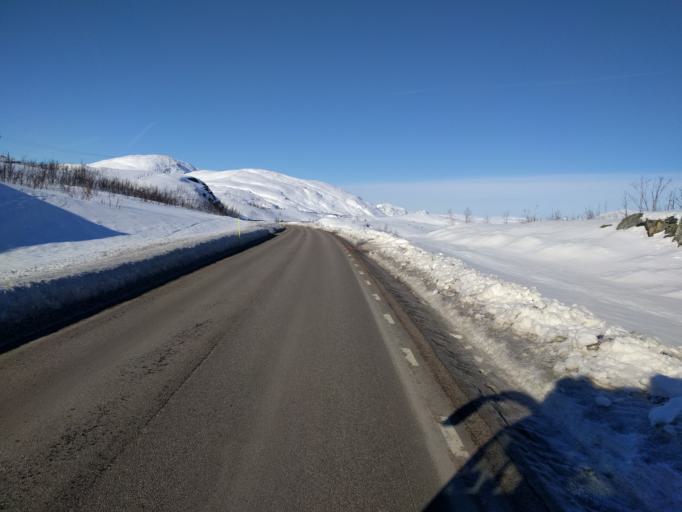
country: NO
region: Troms
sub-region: Bardu
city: Setermoen
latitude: 68.4315
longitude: 18.2187
